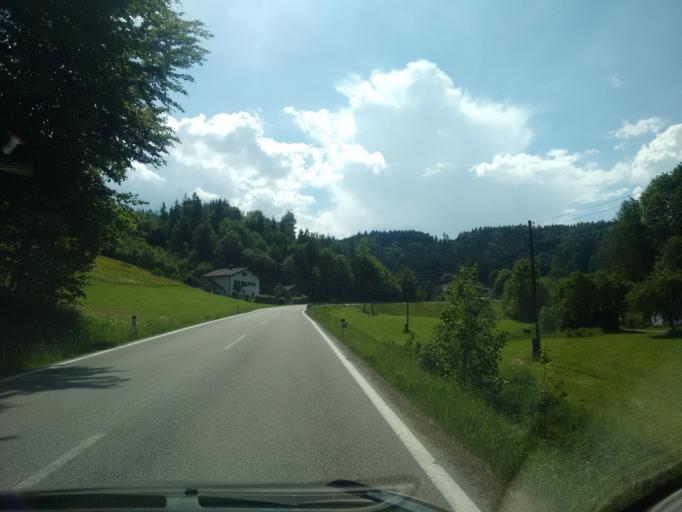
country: AT
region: Upper Austria
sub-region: Politischer Bezirk Kirchdorf an der Krems
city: Rossleithen
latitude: 47.7122
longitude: 14.2561
